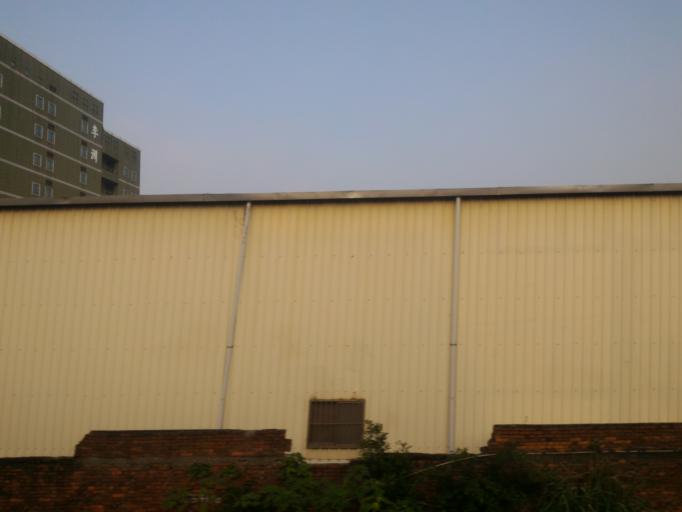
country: TW
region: Taiwan
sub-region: Taoyuan
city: Taoyuan
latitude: 24.9822
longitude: 121.3278
